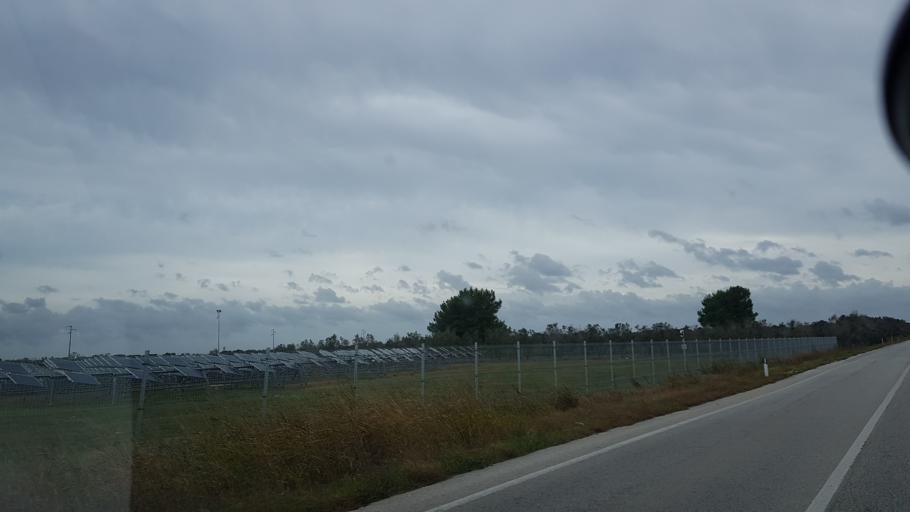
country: IT
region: Apulia
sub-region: Provincia di Lecce
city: Guagnano
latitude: 40.3999
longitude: 17.9163
